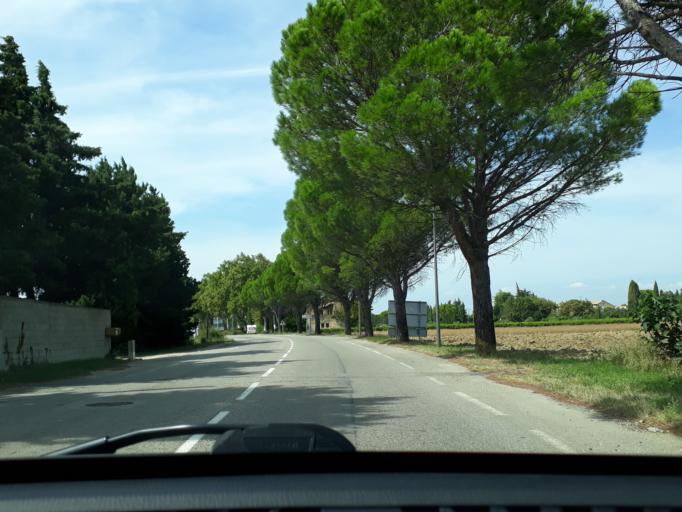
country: FR
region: Provence-Alpes-Cote d'Azur
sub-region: Departement du Vaucluse
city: Sainte-Cecile-les-Vignes
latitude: 44.2473
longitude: 4.8800
